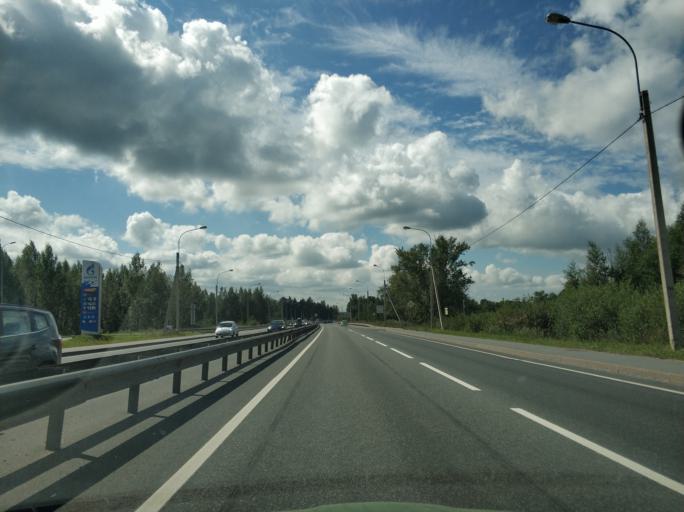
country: RU
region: Leningrad
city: Vsevolozhsk
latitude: 60.0163
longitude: 30.5912
